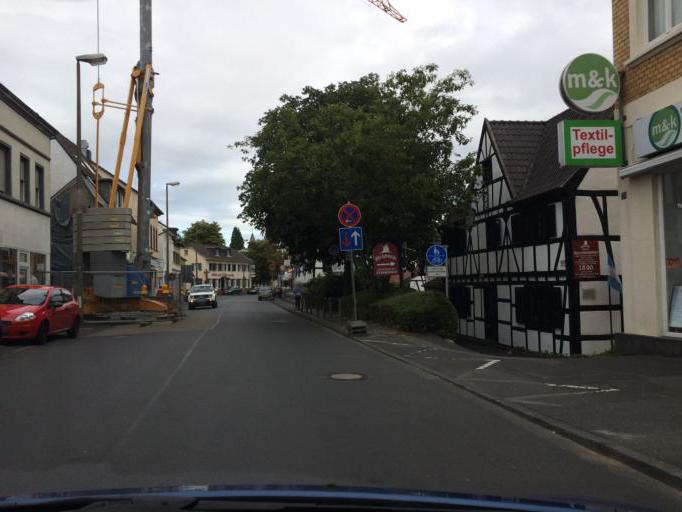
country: DE
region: North Rhine-Westphalia
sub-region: Regierungsbezirk Koln
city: Konigswinter
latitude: 50.6615
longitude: 7.1916
